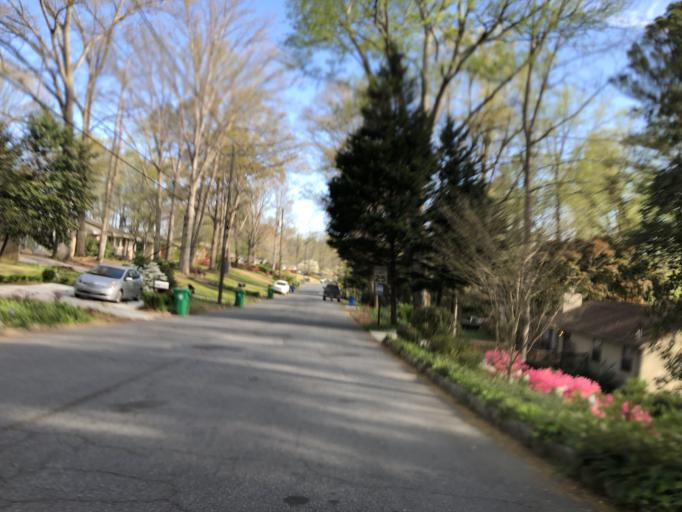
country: US
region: Georgia
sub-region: DeKalb County
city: North Decatur
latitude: 33.8028
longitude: -84.2990
